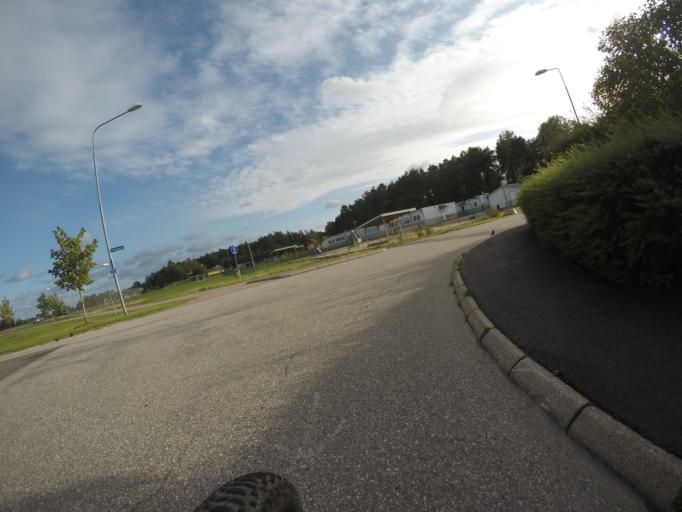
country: SE
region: Vaestmanland
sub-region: Kopings Kommun
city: Koping
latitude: 59.5169
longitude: 16.0105
